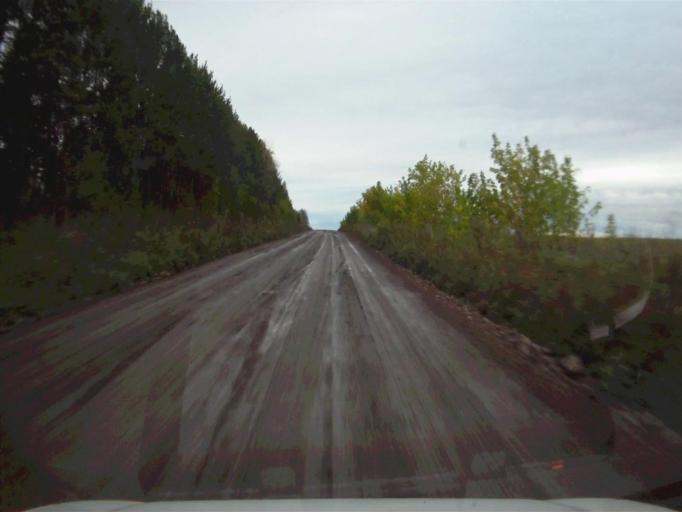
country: RU
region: Sverdlovsk
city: Mikhaylovsk
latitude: 56.1549
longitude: 59.2610
